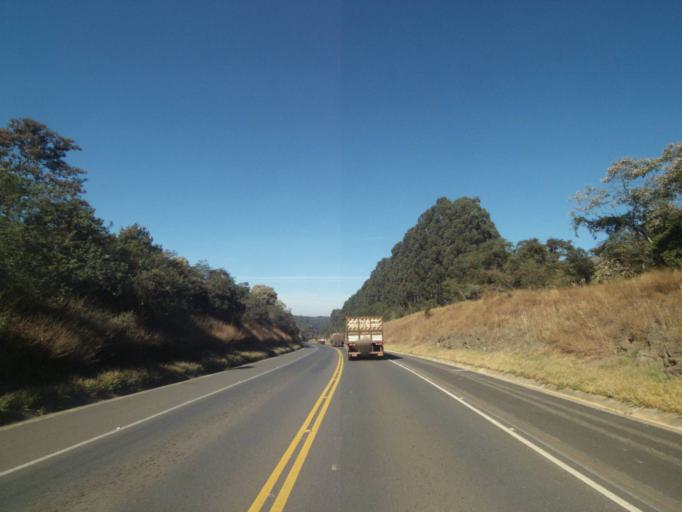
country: BR
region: Parana
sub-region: Tibagi
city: Tibagi
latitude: -24.5637
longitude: -50.4545
